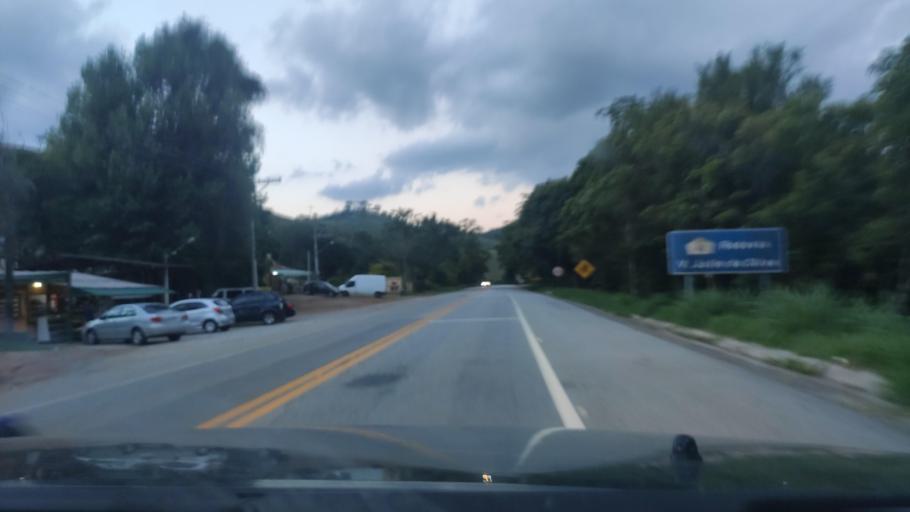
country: BR
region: Sao Paulo
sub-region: Campos Do Jordao
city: Campos do Jordao
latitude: -22.8152
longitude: -45.7527
